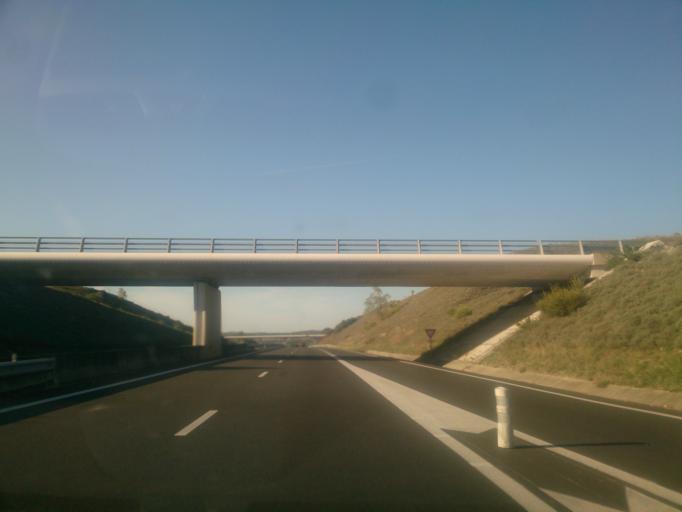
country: FR
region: Midi-Pyrenees
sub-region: Departement du Lot
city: Cahors
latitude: 44.5300
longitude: 1.5125
